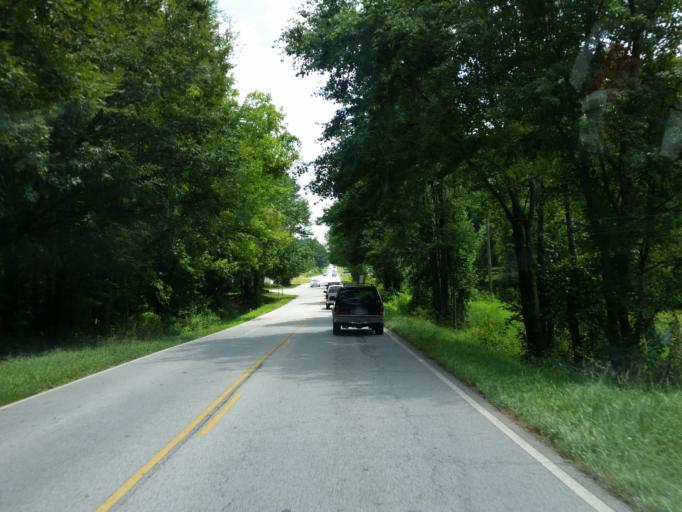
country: US
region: Georgia
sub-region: Henry County
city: Stockbridge
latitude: 33.4946
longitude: -84.2406
